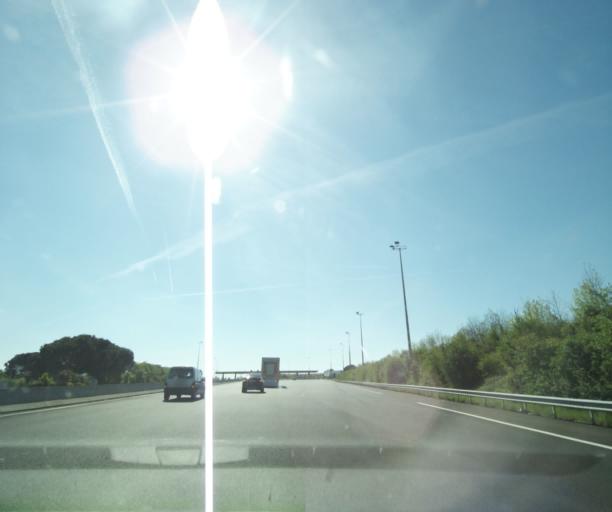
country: FR
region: Midi-Pyrenees
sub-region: Departement du Tarn-et-Garonne
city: Albias
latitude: 44.0516
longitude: 1.4133
